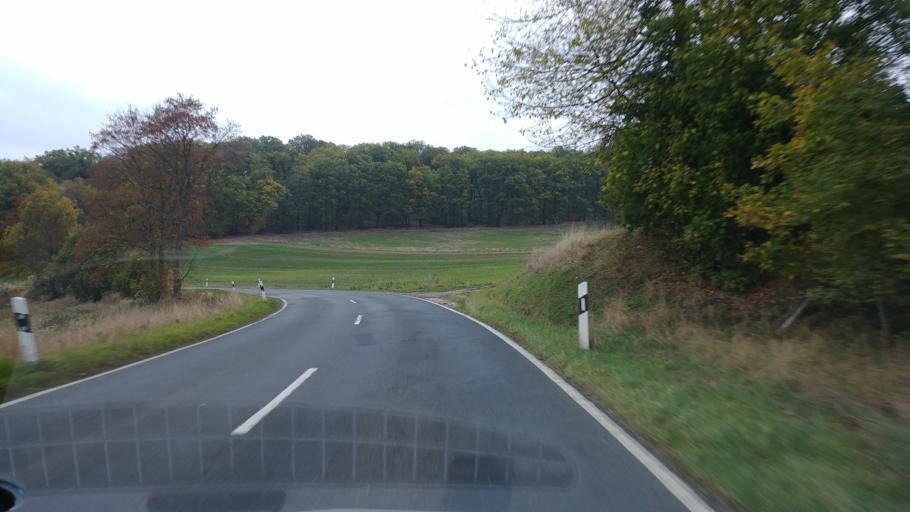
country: DE
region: Hesse
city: Taunusstein
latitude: 50.1707
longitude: 8.1511
